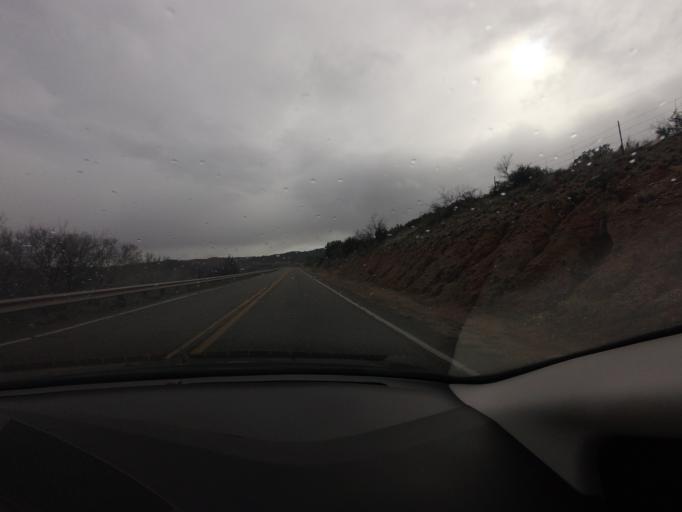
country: US
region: Arizona
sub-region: Yavapai County
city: Lake Montezuma
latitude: 34.6576
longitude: -111.8219
